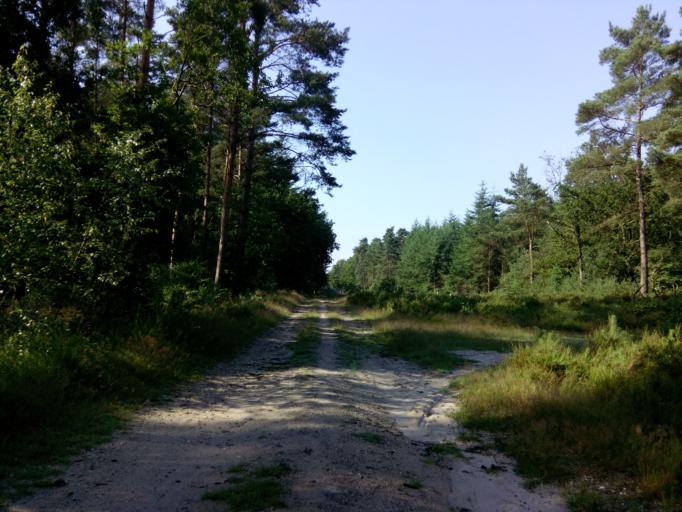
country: NL
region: Utrecht
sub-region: Gemeente Utrechtse Heuvelrug
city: Maarn
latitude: 52.0876
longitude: 5.3550
